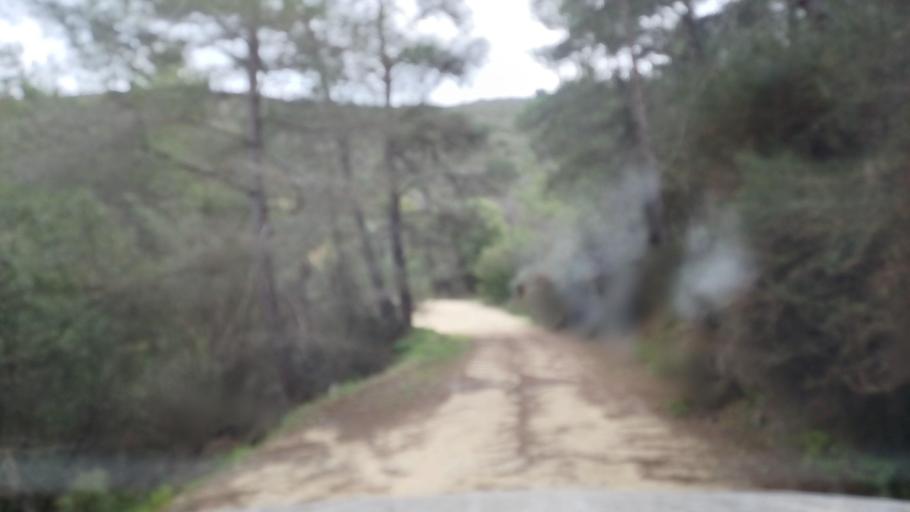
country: CY
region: Limassol
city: Pachna
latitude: 34.7702
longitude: 32.6949
